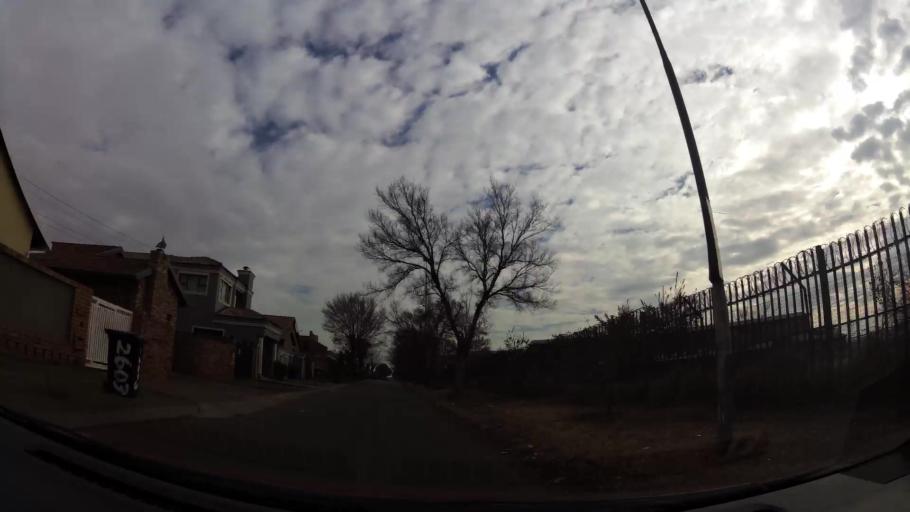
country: ZA
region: Gauteng
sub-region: City of Johannesburg Metropolitan Municipality
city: Soweto
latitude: -26.2699
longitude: 27.8374
